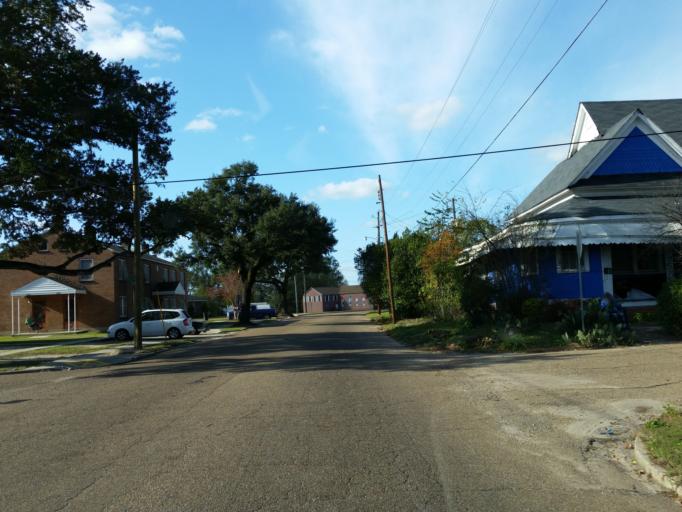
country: US
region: Mississippi
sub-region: Forrest County
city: Hattiesburg
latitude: 31.3316
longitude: -89.2861
